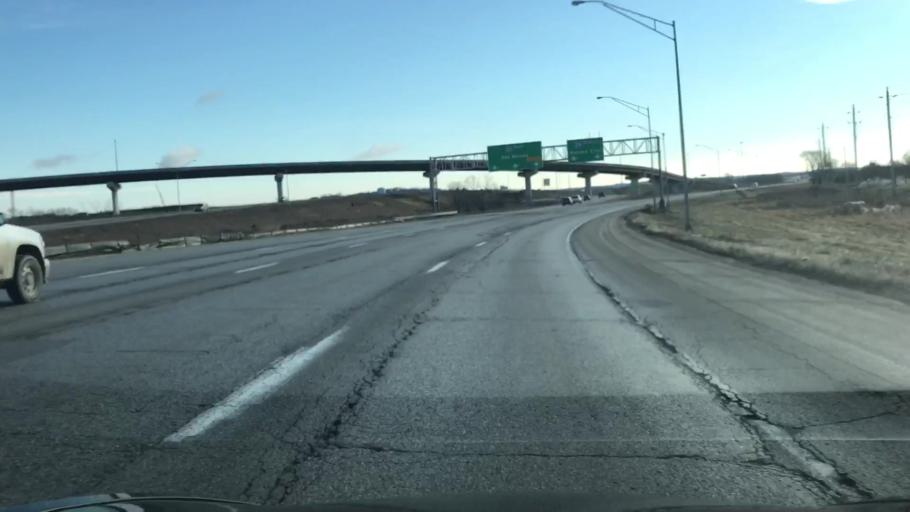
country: US
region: Iowa
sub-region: Pottawattamie County
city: Council Bluffs
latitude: 41.2313
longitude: -95.8447
